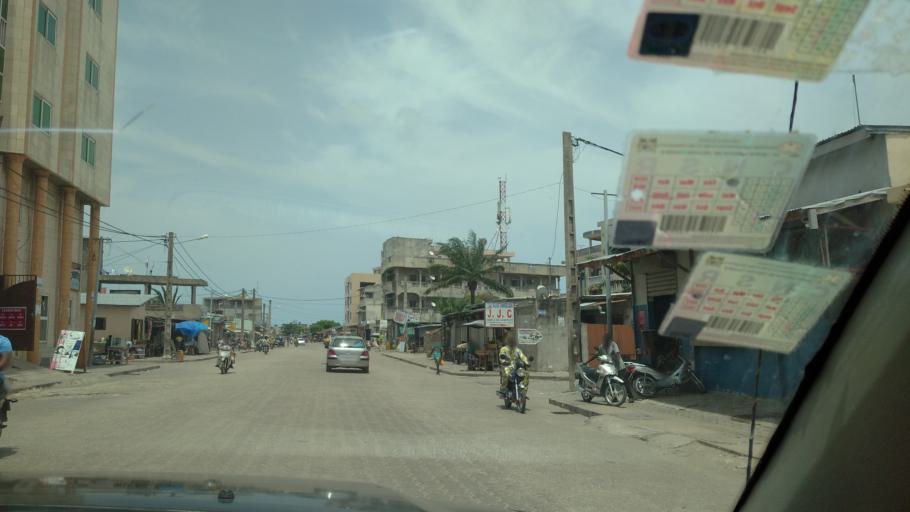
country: BJ
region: Littoral
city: Cotonou
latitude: 6.3911
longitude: 2.4566
